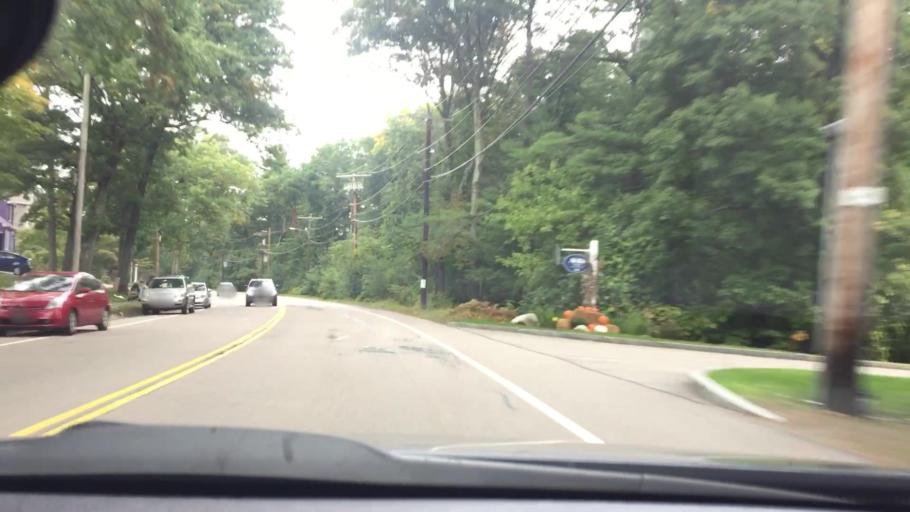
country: US
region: Massachusetts
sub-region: Norfolk County
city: Needham
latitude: 42.2794
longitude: -71.2040
